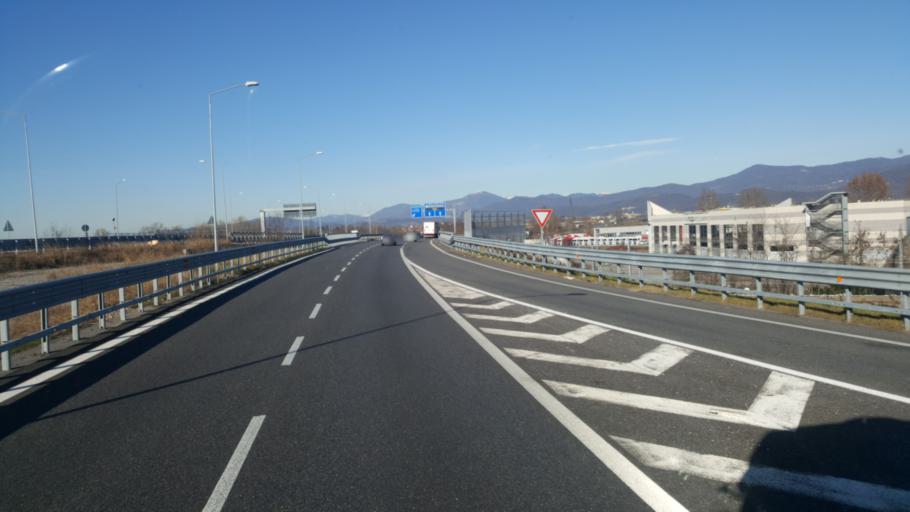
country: IT
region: Lombardy
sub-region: Provincia di Brescia
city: Castegnato
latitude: 45.5480
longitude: 10.1330
